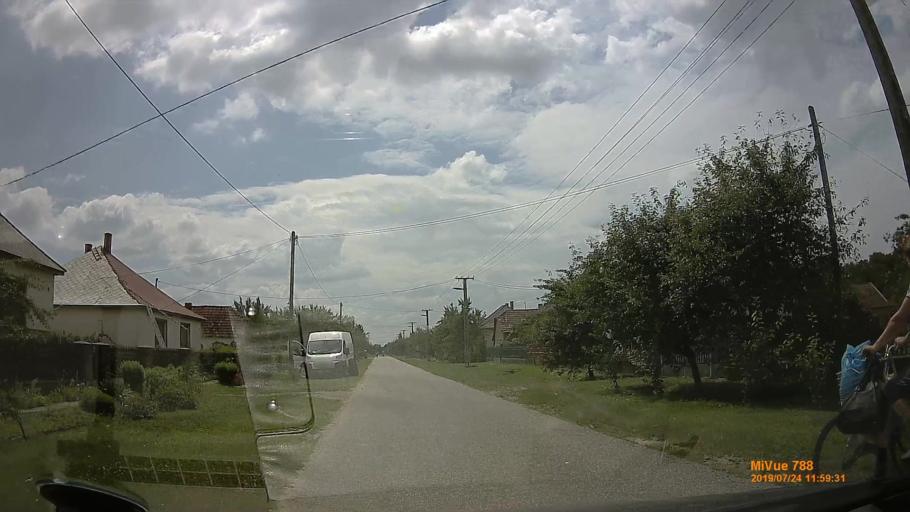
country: HU
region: Szabolcs-Szatmar-Bereg
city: Tarpa
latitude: 48.2022
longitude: 22.4510
